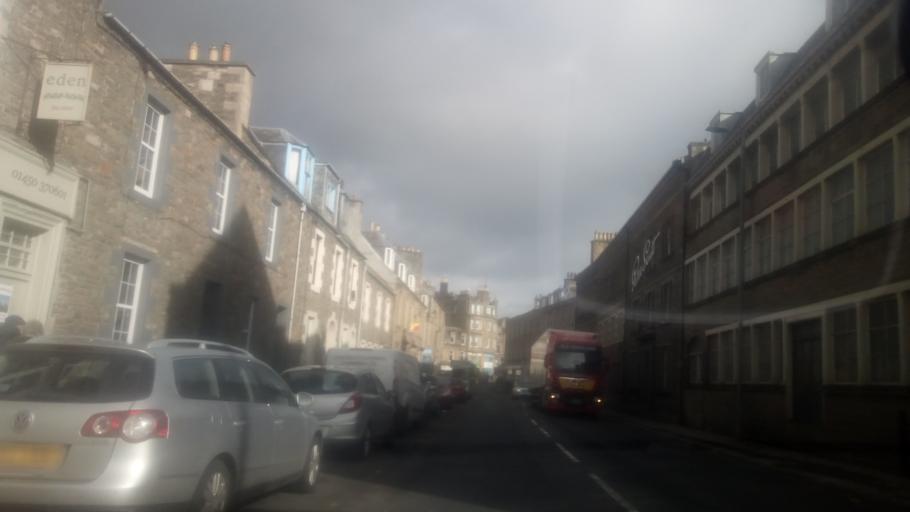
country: GB
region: Scotland
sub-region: The Scottish Borders
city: Hawick
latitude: 55.4213
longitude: -2.7912
